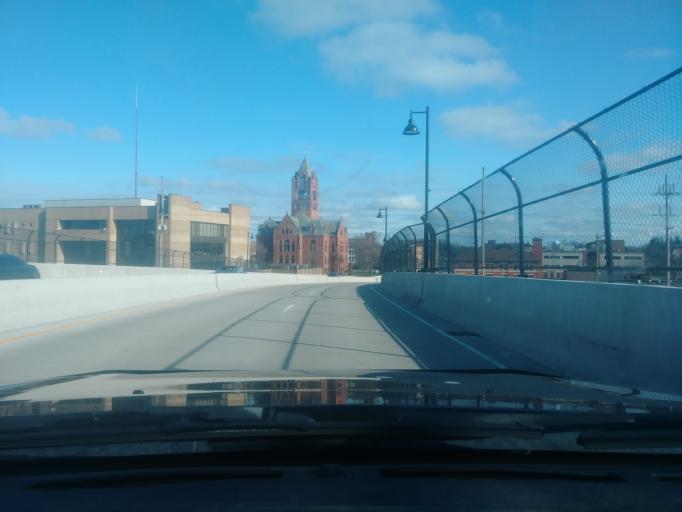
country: US
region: Indiana
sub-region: LaPorte County
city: LaPorte
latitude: 41.6126
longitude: -86.7247
